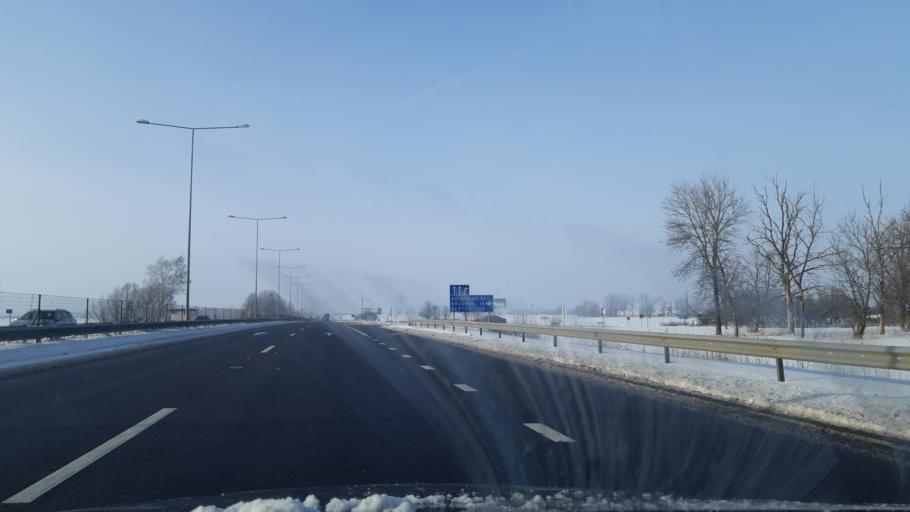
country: LT
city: Kaisiadorys
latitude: 54.8416
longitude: 24.3436
